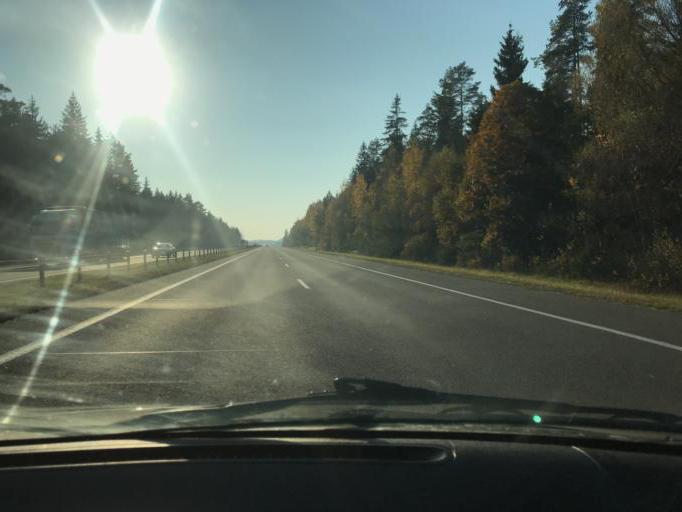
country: BY
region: Minsk
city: Krupki
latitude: 54.3274
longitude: 29.0816
